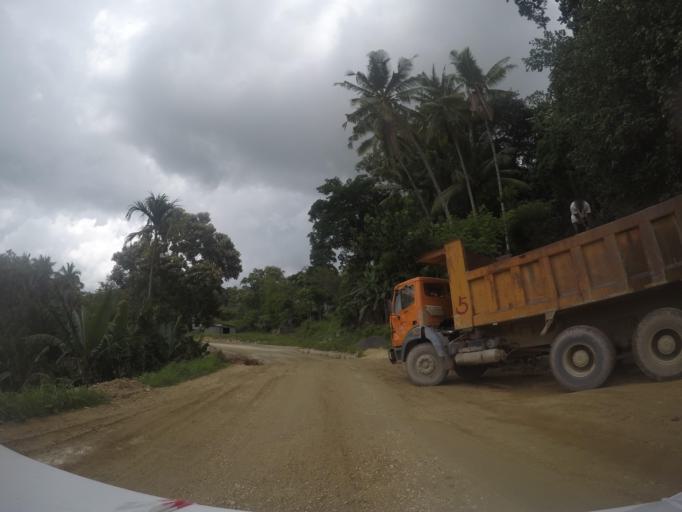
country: TL
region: Baucau
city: Venilale
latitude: -8.6035
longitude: 126.3826
